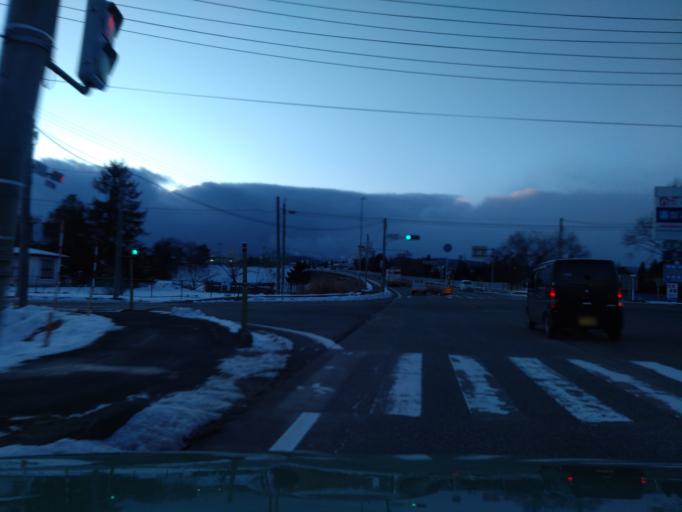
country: JP
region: Iwate
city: Shizukuishi
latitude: 39.7030
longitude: 140.9700
